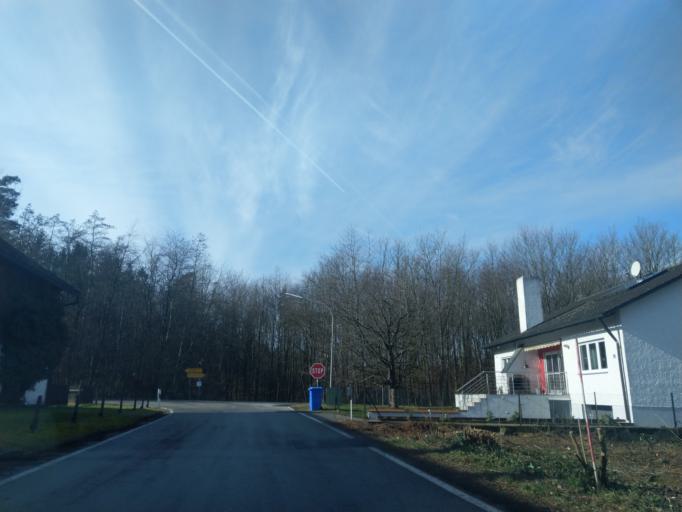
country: DE
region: Bavaria
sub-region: Lower Bavaria
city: Buchhofen
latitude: 48.6680
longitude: 12.9187
